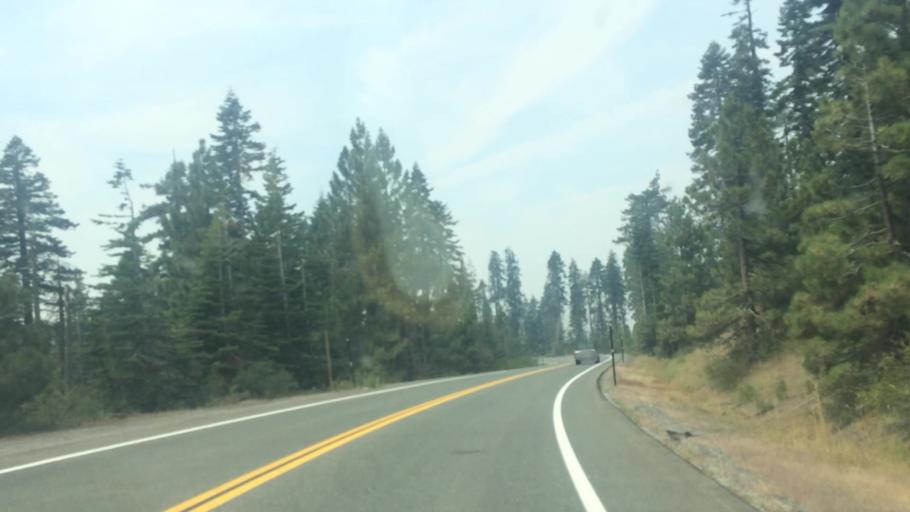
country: US
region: California
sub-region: Calaveras County
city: Arnold
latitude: 38.5858
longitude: -120.2395
